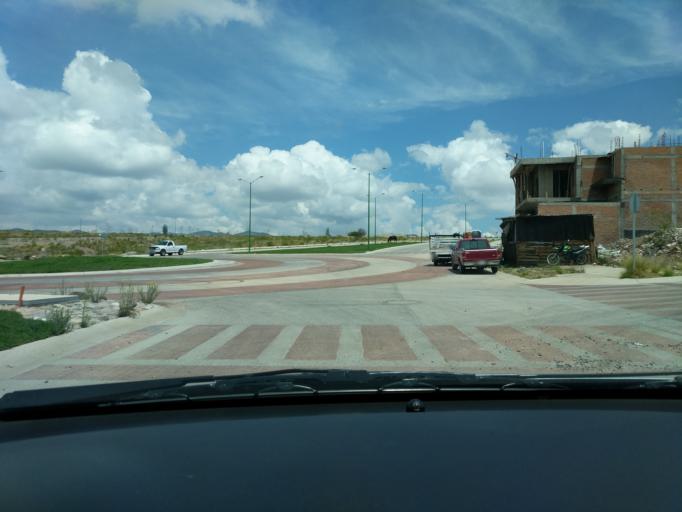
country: MX
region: San Luis Potosi
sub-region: Mexquitic de Carmona
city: Guadalupe Victoria
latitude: 22.1551
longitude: -101.0514
